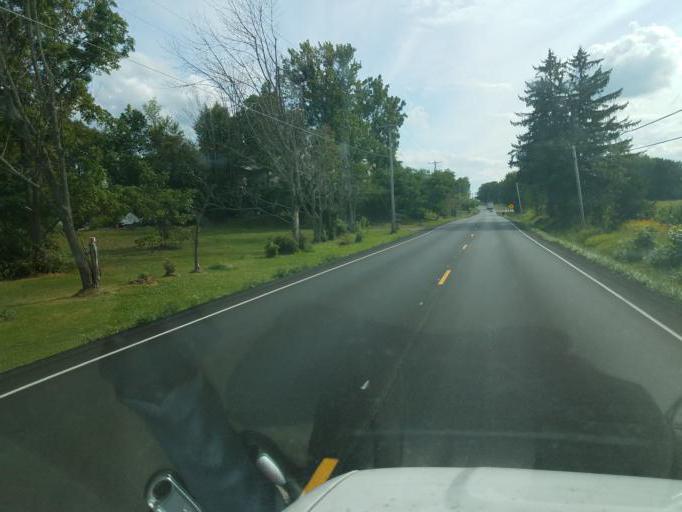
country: US
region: Ohio
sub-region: Stark County
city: Hartville
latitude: 40.9697
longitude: -81.2505
